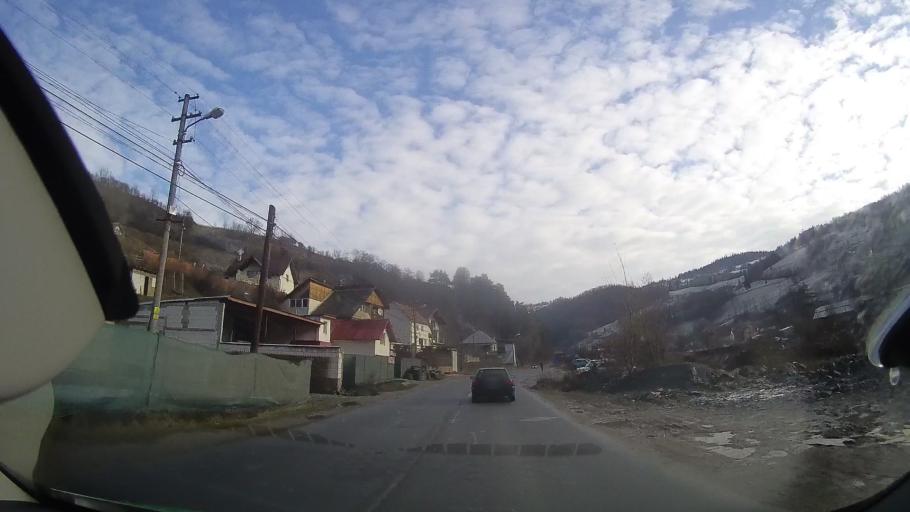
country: RO
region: Alba
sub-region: Oras Campeni
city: Campeni
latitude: 46.3600
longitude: 23.0706
